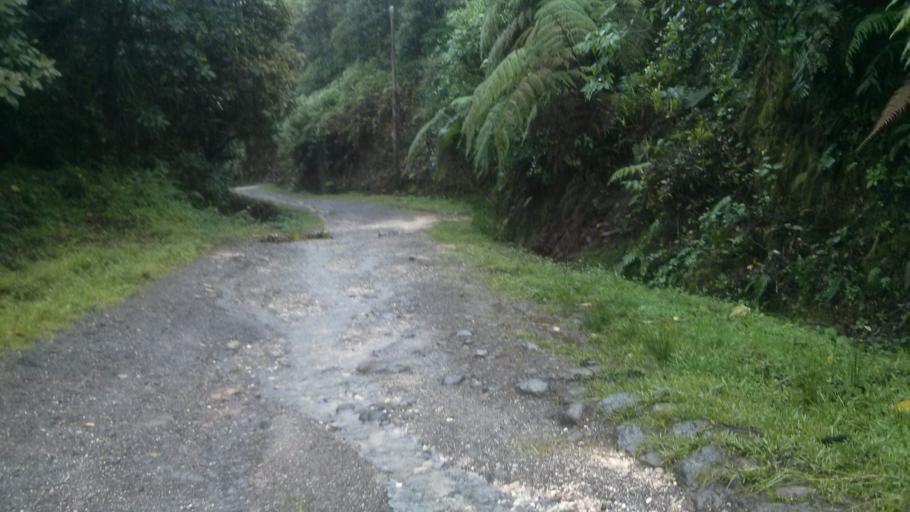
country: CR
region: San Jose
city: Ipis
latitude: 10.0286
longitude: -83.9431
